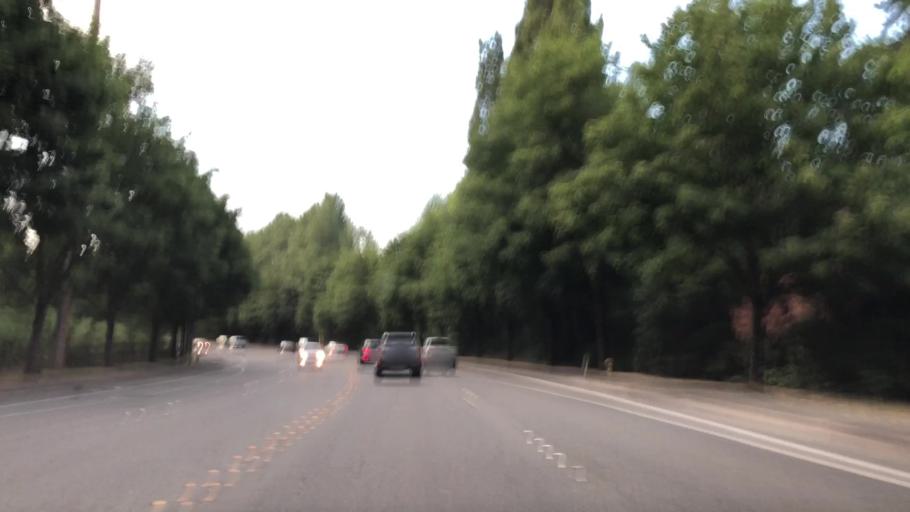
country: US
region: Washington
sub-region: King County
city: Redmond
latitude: 47.6892
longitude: -122.0921
